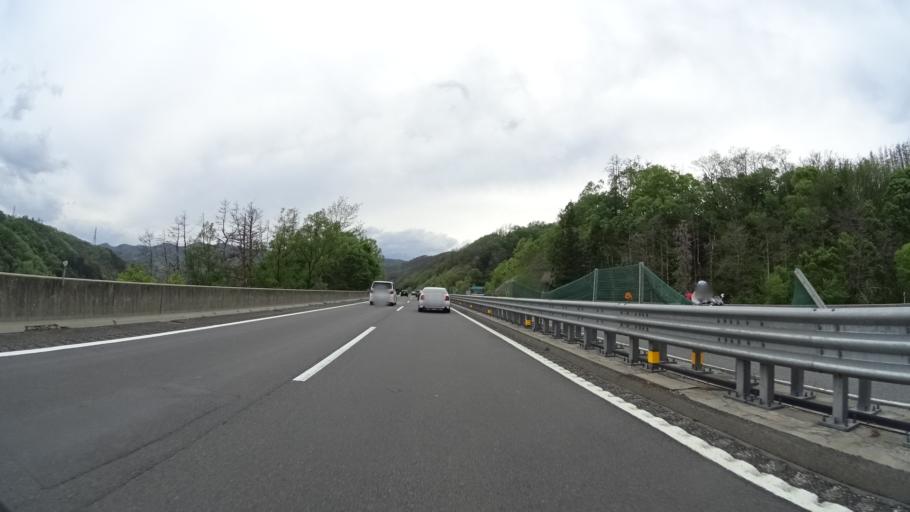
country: JP
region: Nagano
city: Toyoshina
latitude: 36.3547
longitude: 137.9758
